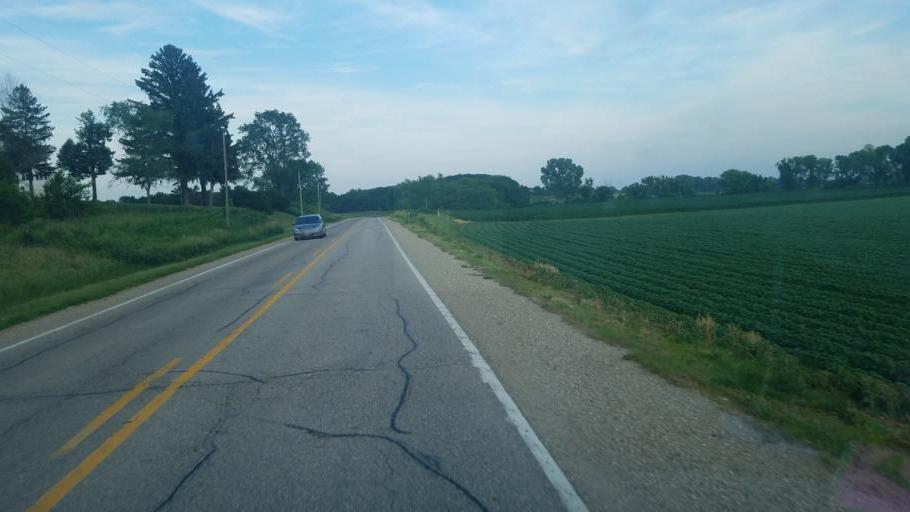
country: US
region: Iowa
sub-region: Tama County
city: Tama
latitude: 41.9595
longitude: -92.4314
